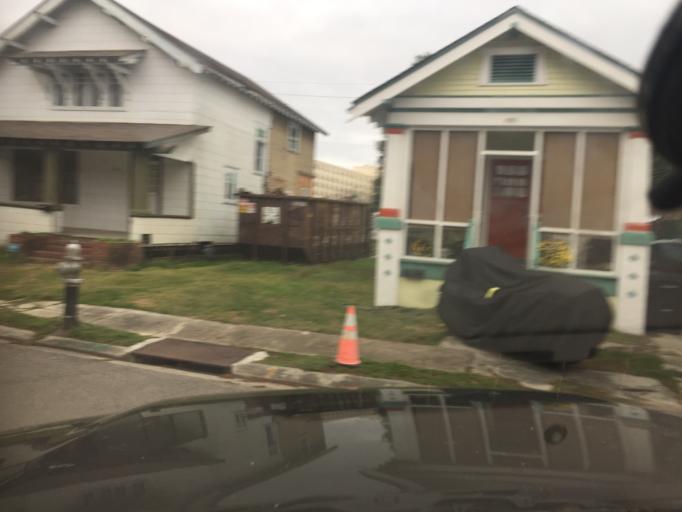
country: US
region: Louisiana
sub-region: Orleans Parish
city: New Orleans
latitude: 29.9842
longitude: -90.0859
